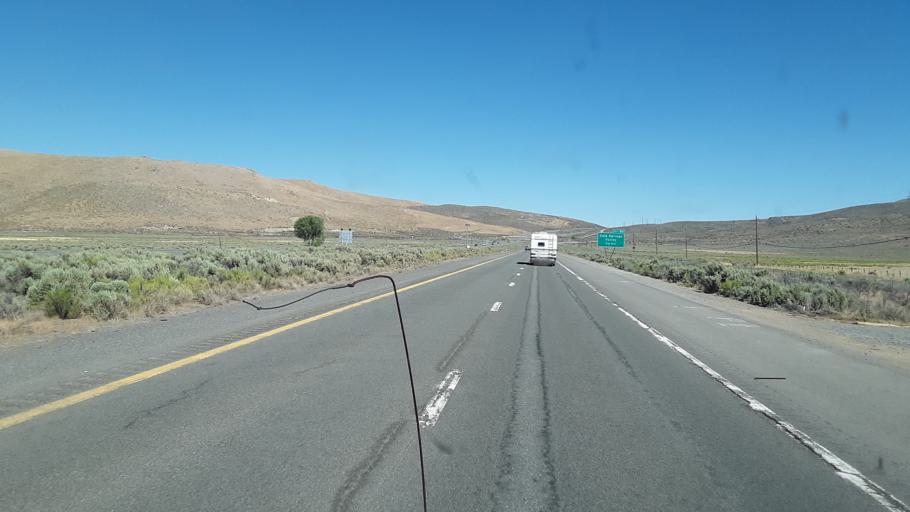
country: US
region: Nevada
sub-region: Washoe County
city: Cold Springs
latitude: 39.6491
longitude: -119.9742
